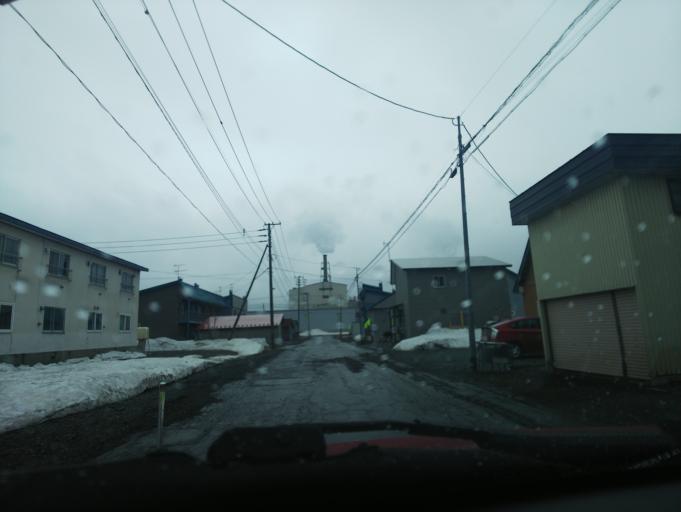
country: JP
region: Hokkaido
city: Nayoro
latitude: 44.3425
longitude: 142.4604
